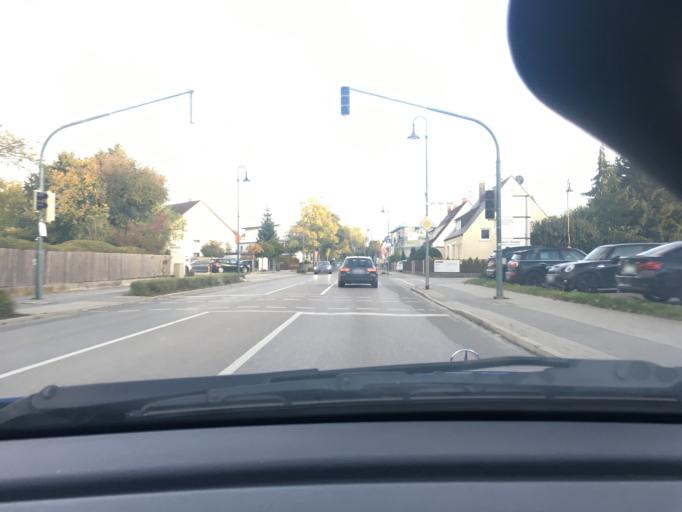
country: DE
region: Bavaria
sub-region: Swabia
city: Stadtbergen
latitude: 48.3887
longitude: 10.8389
